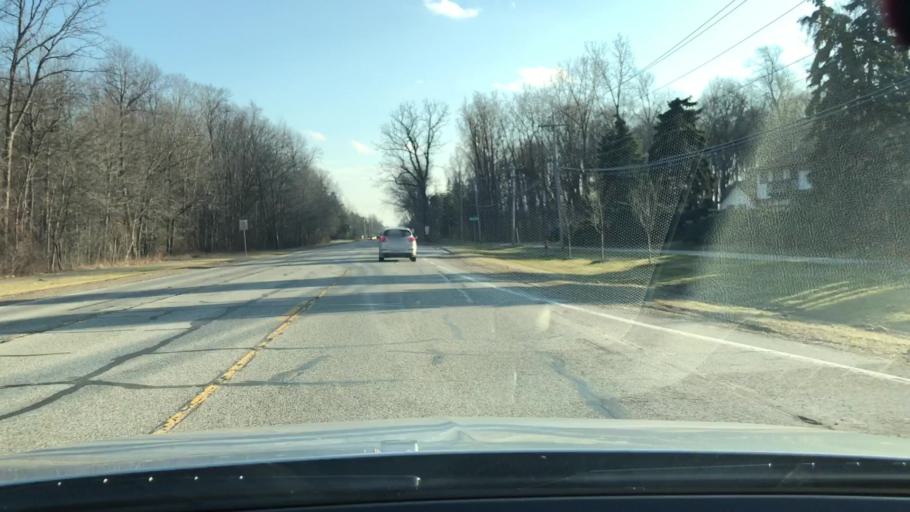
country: US
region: Michigan
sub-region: Oakland County
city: Rochester
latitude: 42.6483
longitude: -83.1123
